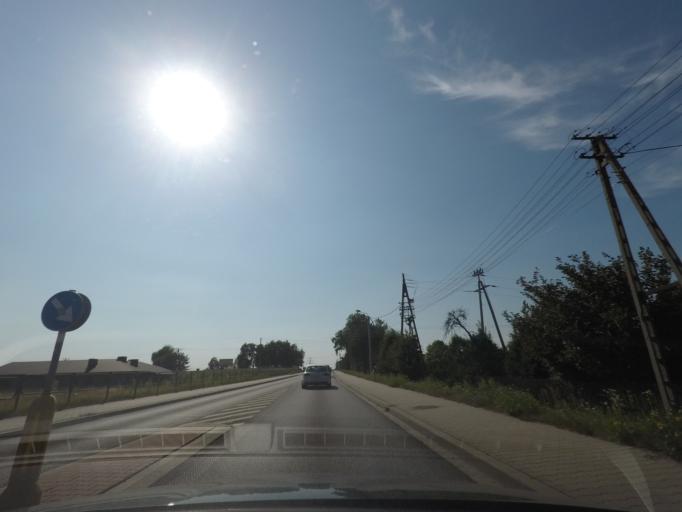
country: PL
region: Silesian Voivodeship
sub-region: Powiat pszczynski
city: Rudziczka
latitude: 50.0356
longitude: 18.7637
